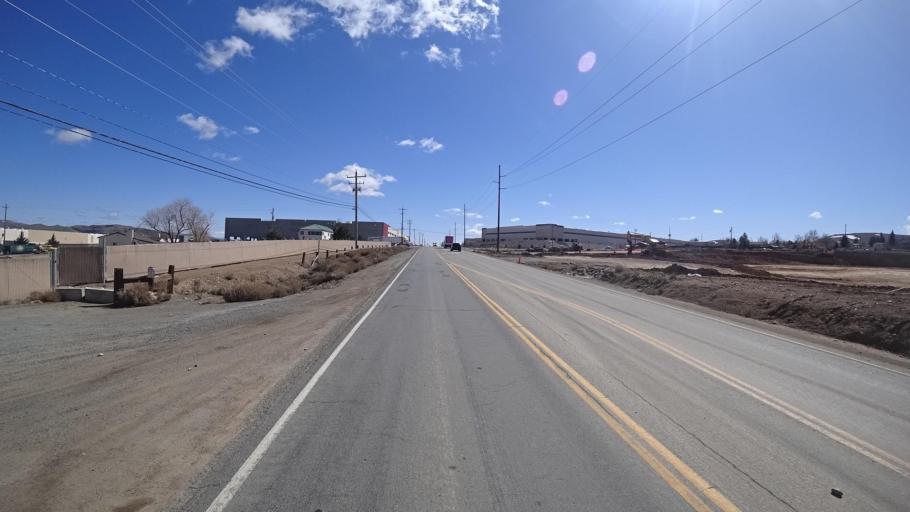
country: US
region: Nevada
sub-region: Washoe County
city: Lemmon Valley
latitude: 39.6090
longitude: -119.8656
